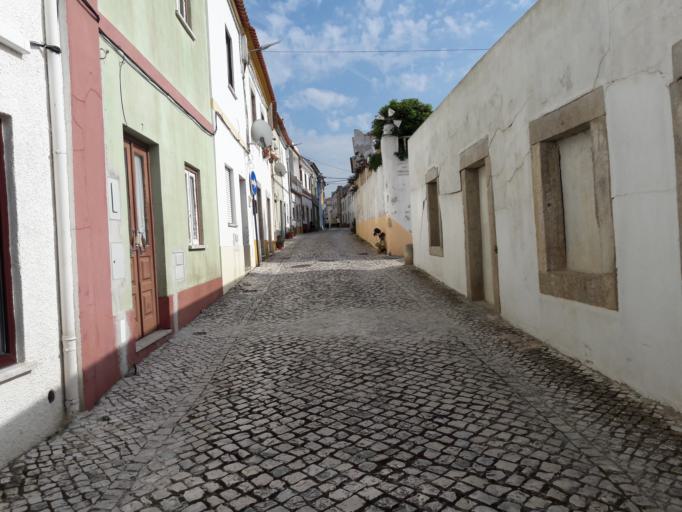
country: PT
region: Leiria
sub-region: Peniche
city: Atouguia da Baleia
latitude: 39.3390
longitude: -9.3253
